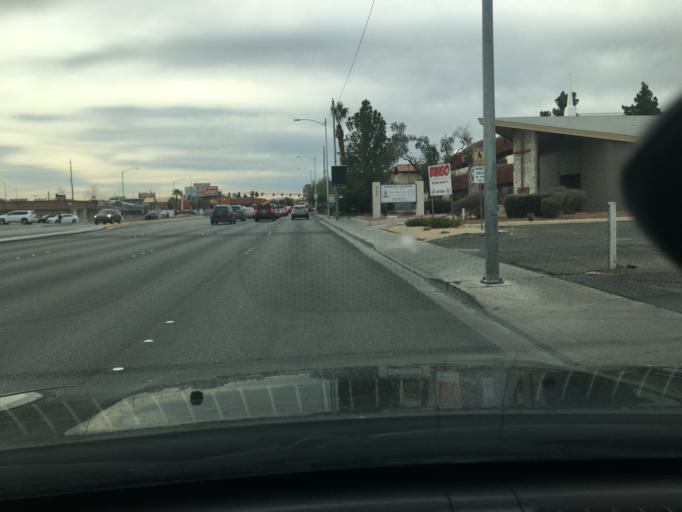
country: US
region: Nevada
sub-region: Clark County
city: Spring Valley
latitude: 36.1611
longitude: -115.2062
